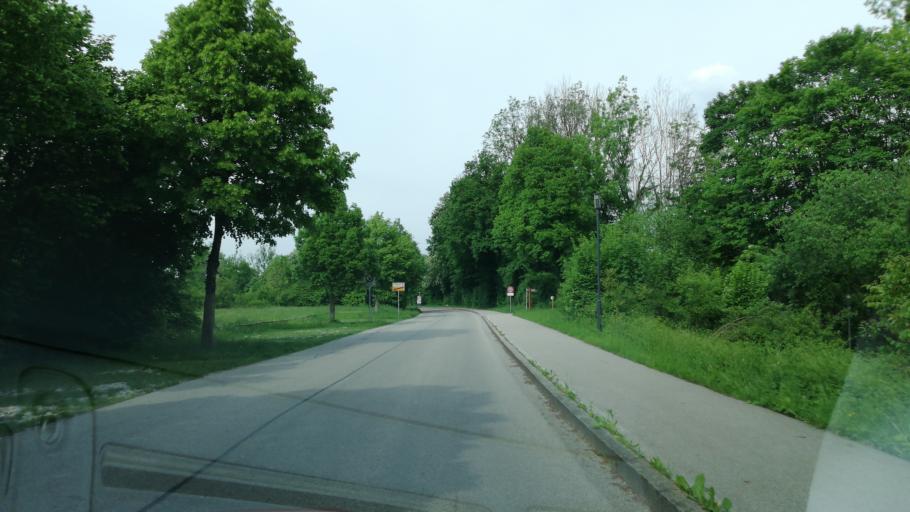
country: DE
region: Bavaria
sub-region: Upper Bavaria
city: Mehring
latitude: 48.1308
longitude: 12.7895
